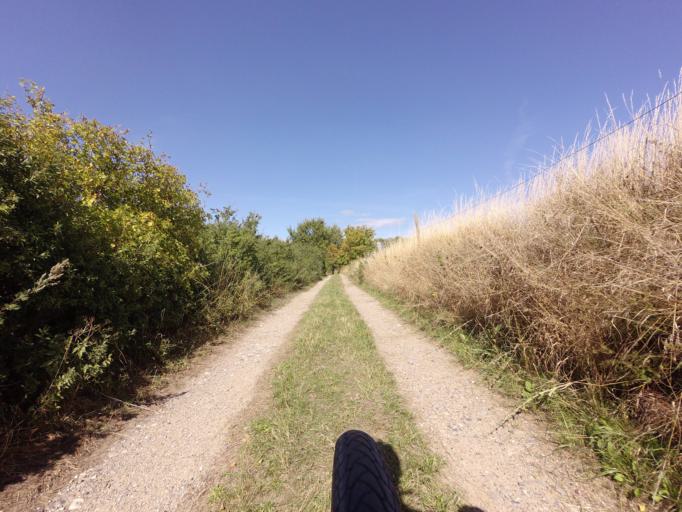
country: DK
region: Zealand
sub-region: Vordingborg Kommune
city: Stege
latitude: 55.0212
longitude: 12.4508
